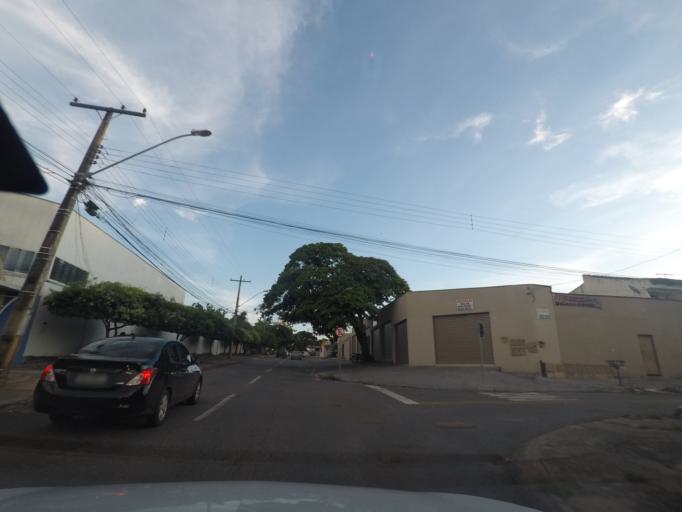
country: BR
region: Goias
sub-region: Goiania
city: Goiania
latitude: -16.6937
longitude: -49.2861
